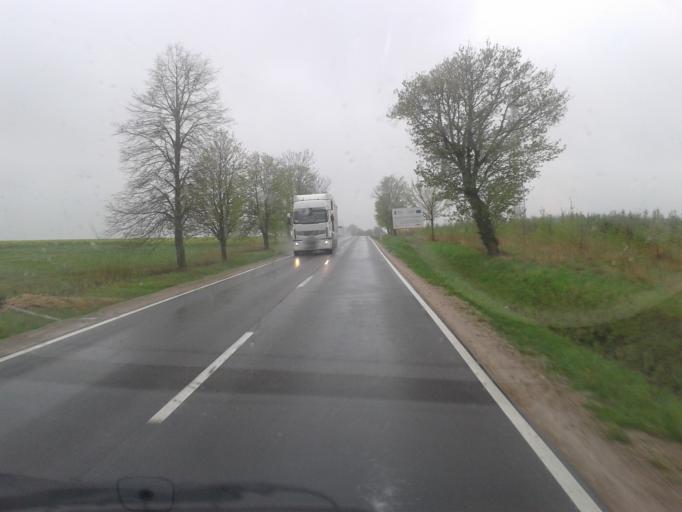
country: PL
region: Subcarpathian Voivodeship
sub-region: Powiat lubaczowski
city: Cieszanow
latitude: 50.2581
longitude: 23.1422
